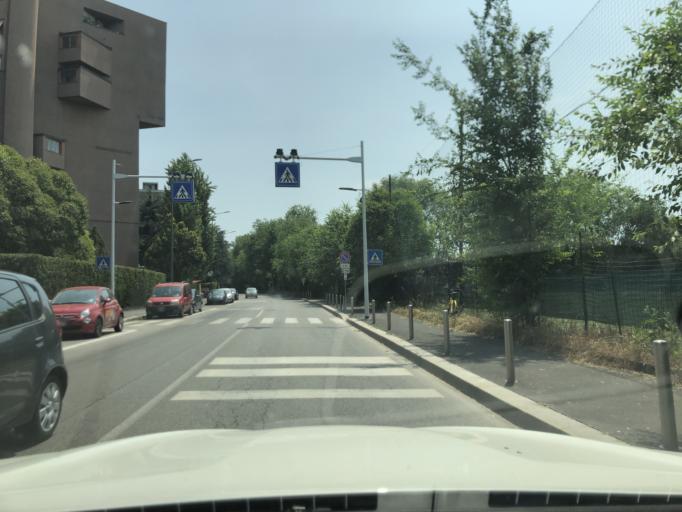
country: IT
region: Lombardy
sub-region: Citta metropolitana di Milano
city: Pero
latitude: 45.4978
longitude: 9.0997
